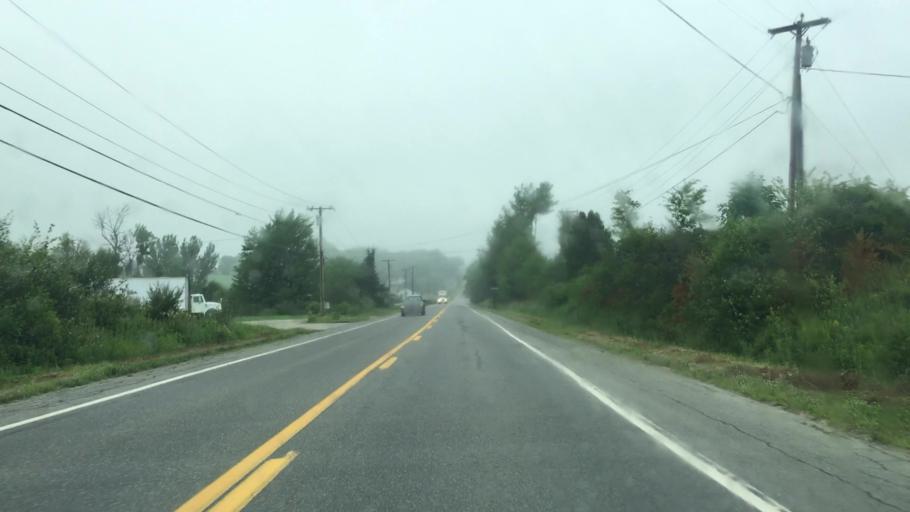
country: US
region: Maine
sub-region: Lincoln County
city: Wiscasset
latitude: 44.0390
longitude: -69.6736
